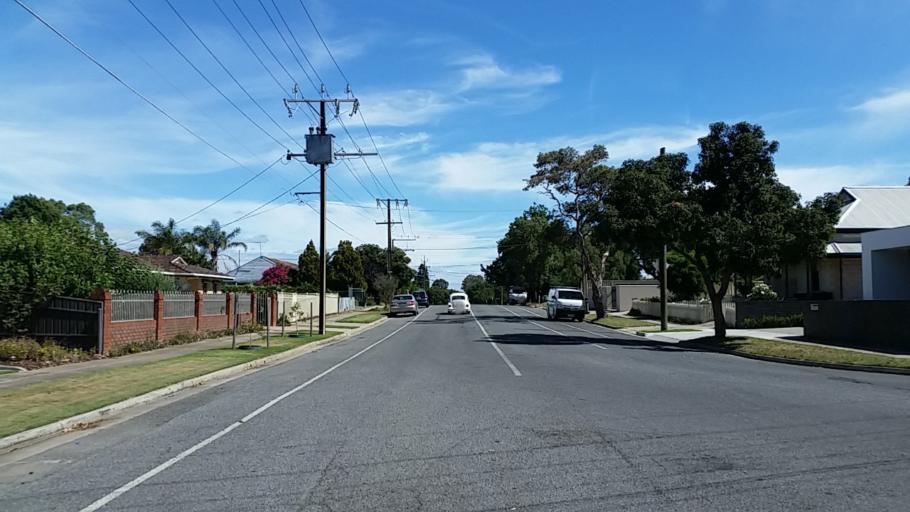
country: AU
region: South Australia
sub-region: Charles Sturt
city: Findon
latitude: -34.9193
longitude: 138.5285
